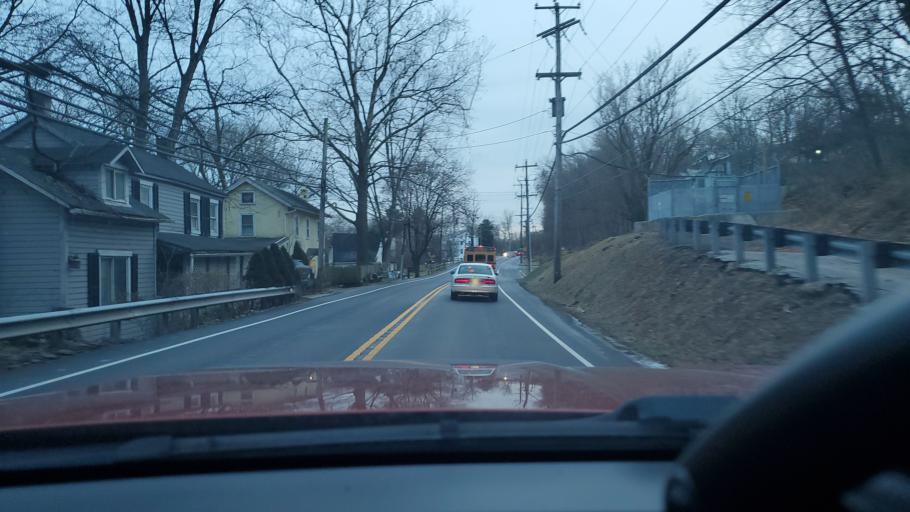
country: US
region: Pennsylvania
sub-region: Montgomery County
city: Schwenksville
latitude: 40.2486
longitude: -75.4584
